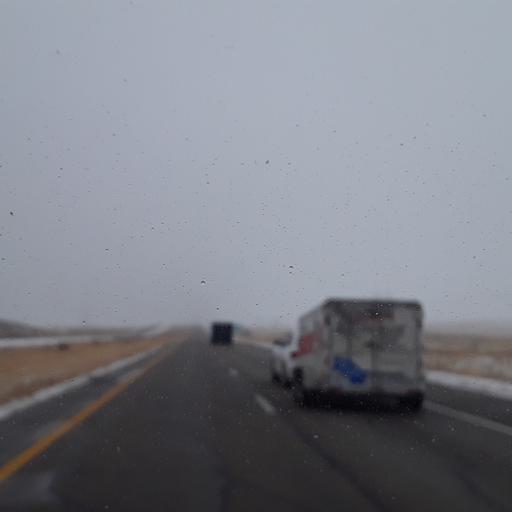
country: US
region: Colorado
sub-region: Logan County
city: Sterling
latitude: 40.7654
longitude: -102.9506
